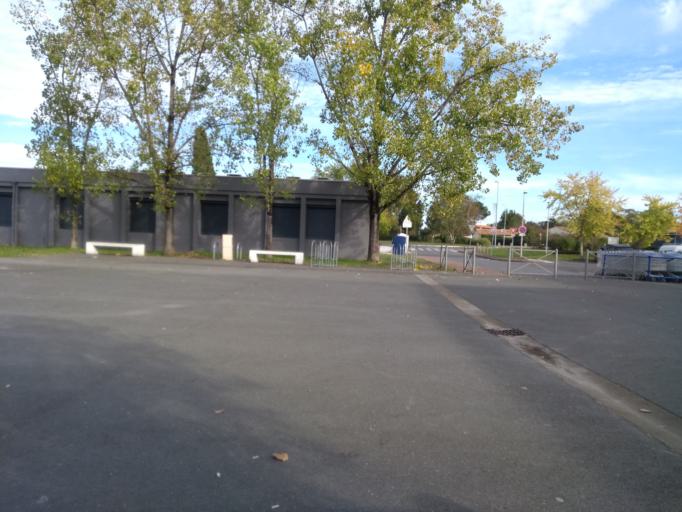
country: FR
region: Aquitaine
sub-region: Departement de la Gironde
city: Pessac
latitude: 44.7924
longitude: -0.6823
